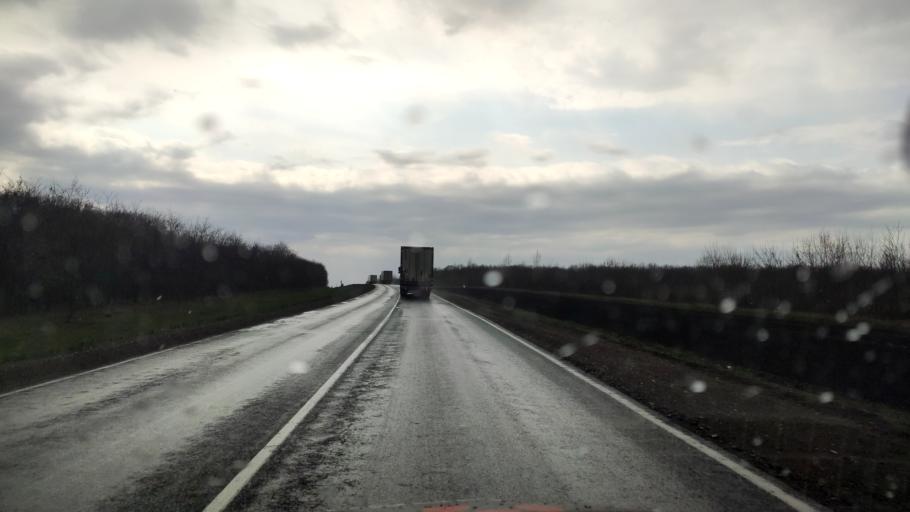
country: RU
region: Voronezj
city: Nizhnedevitsk
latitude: 51.5760
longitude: 38.3066
